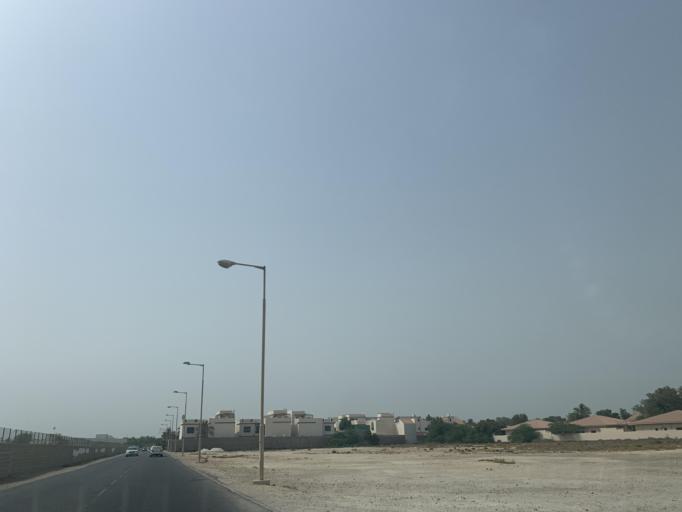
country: BH
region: Manama
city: Jidd Hafs
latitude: 26.1977
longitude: 50.4732
